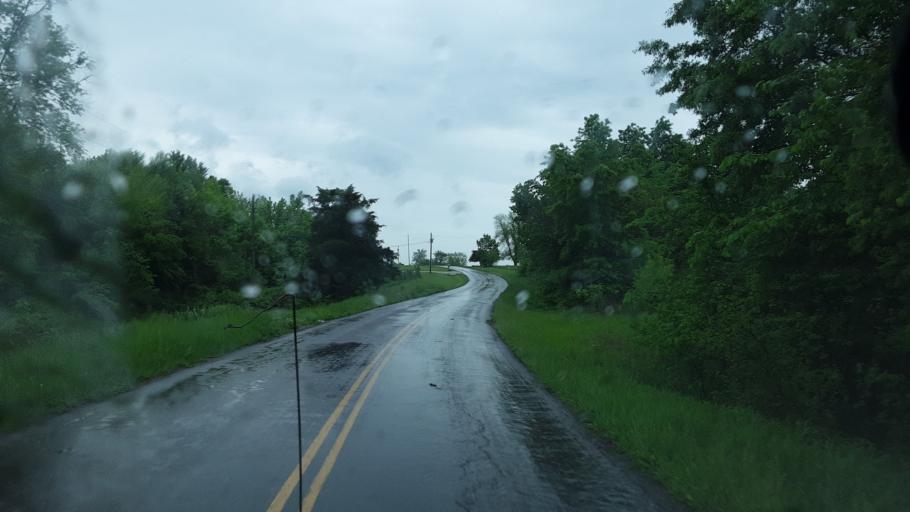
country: US
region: Missouri
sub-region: Randolph County
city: Moberly
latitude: 39.3864
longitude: -92.2483
